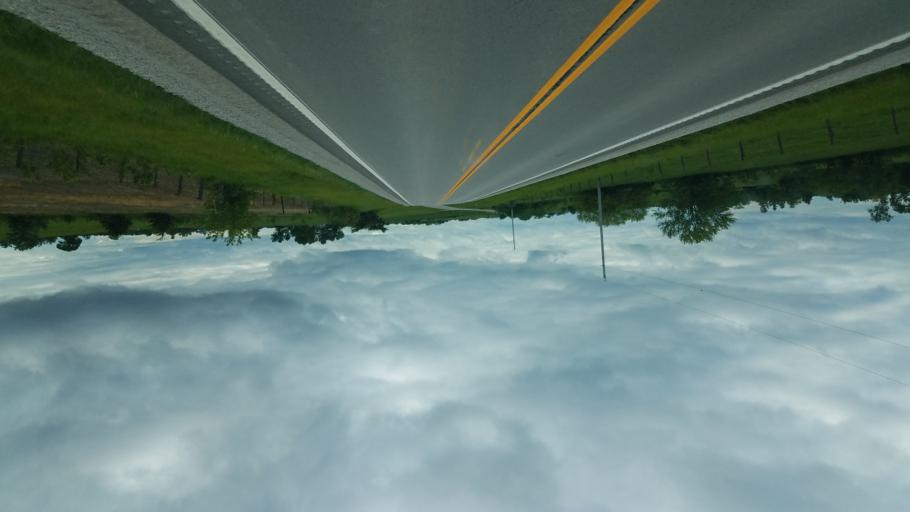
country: US
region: Missouri
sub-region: Harrison County
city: Bethany
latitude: 40.2977
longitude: -93.8191
